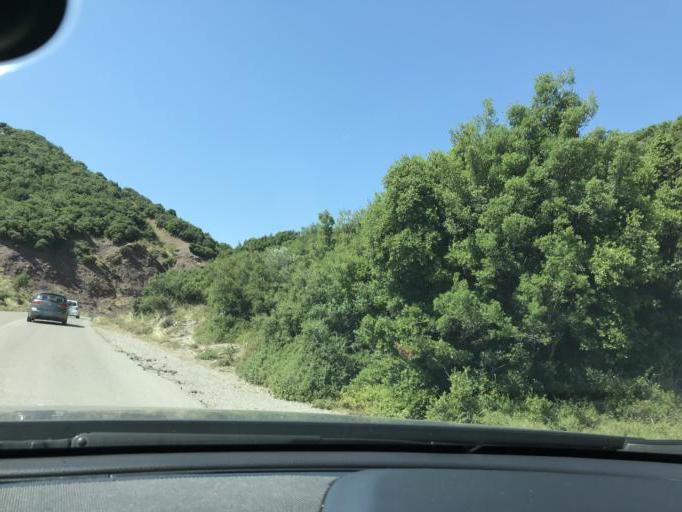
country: GR
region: Central Greece
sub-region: Nomos Voiotias
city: Distomo
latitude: 38.4933
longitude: 22.6971
